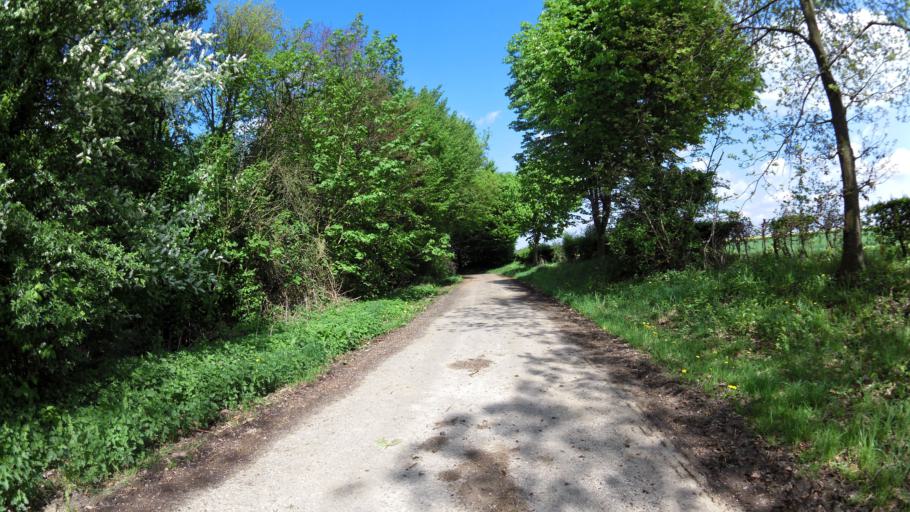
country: NL
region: Limburg
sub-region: Gemeente Kerkrade
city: Kerkrade
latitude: 50.8453
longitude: 6.0380
